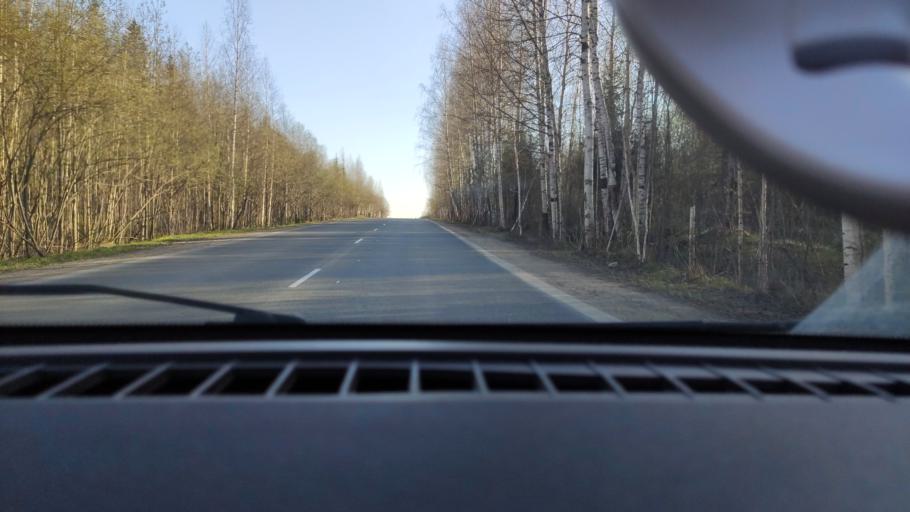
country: RU
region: Perm
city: Polazna
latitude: 58.1205
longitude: 56.4311
